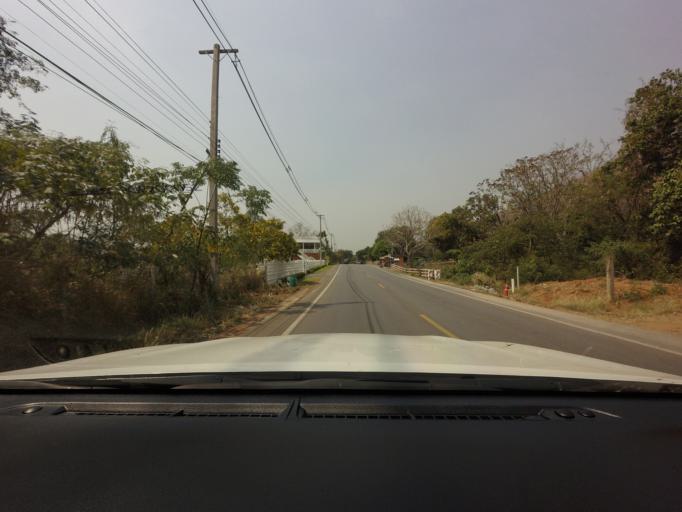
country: TH
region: Sara Buri
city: Muak Lek
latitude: 14.5896
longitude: 101.2331
